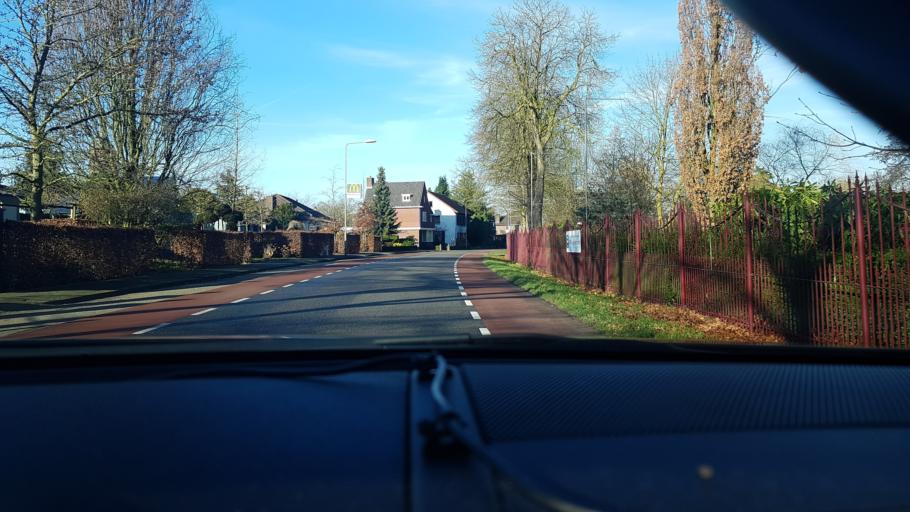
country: NL
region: Limburg
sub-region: Gemeente Peel en Maas
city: Maasbree
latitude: 51.3177
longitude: 6.0039
